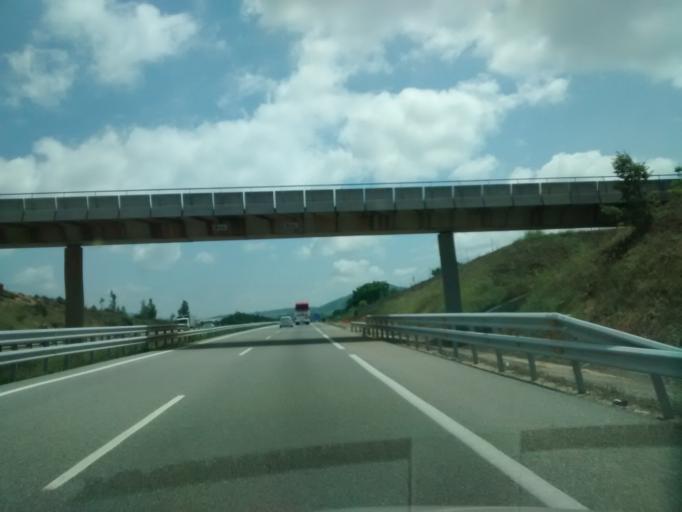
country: ES
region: Castille and Leon
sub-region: Provincia de Leon
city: Camponaraya
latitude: 42.5842
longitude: -6.6443
